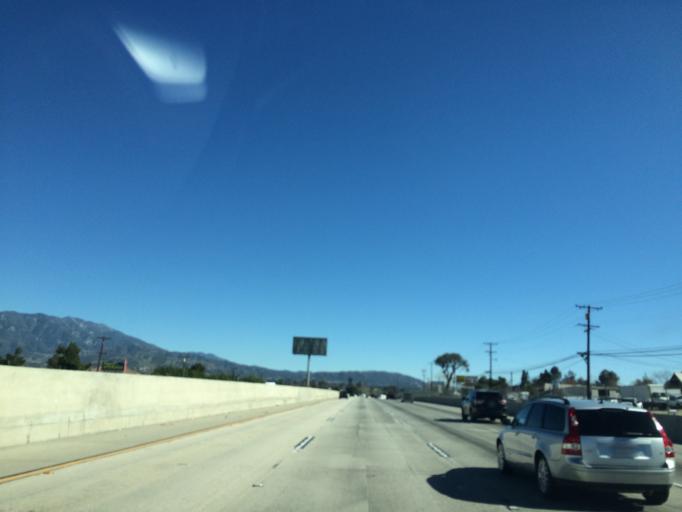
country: US
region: California
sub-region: San Bernardino County
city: Mentone
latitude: 34.0245
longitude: -117.1119
